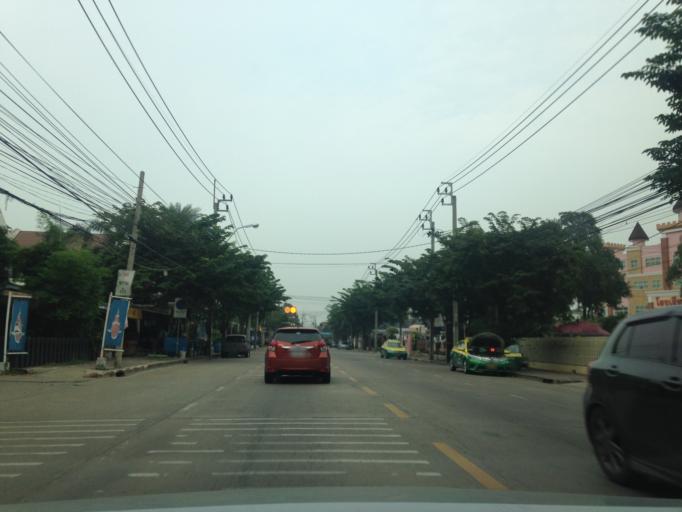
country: TH
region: Bangkok
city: Lat Phrao
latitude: 13.8338
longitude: 100.6262
